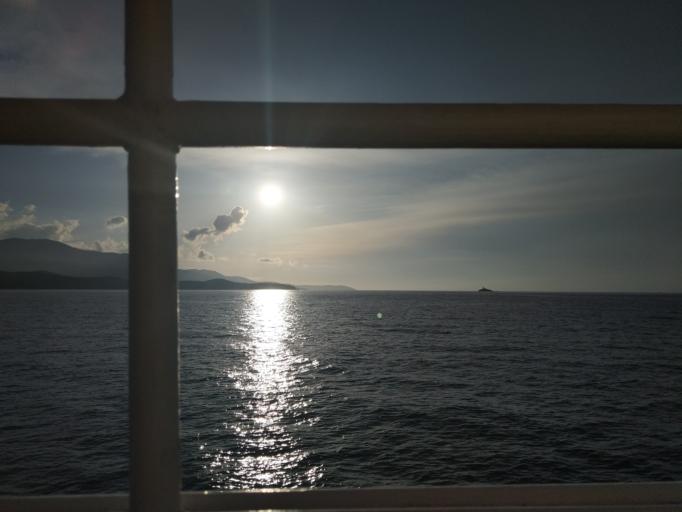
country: AL
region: Vlore
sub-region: Rrethi i Sarandes
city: Xarre
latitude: 39.7791
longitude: 19.9812
